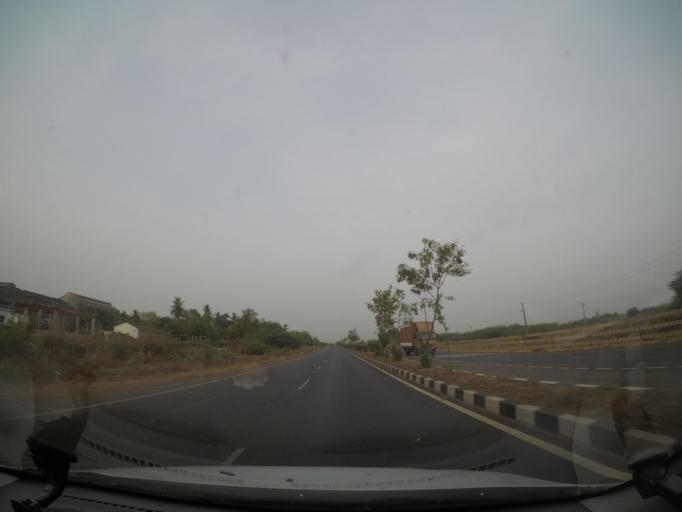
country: IN
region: Andhra Pradesh
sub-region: Krishna
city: Gannavaram
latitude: 16.6233
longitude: 80.9354
